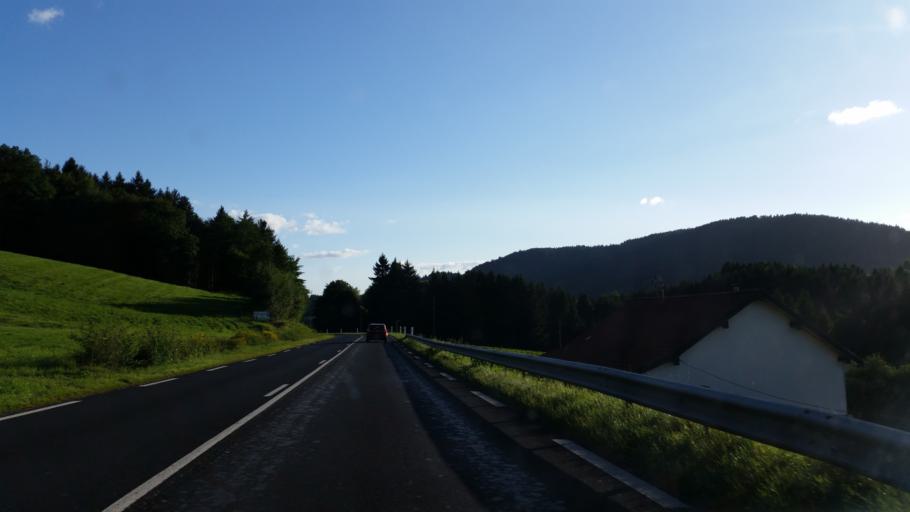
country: FR
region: Lorraine
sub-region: Departement des Vosges
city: Le Syndicat
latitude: 48.0473
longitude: 6.6852
